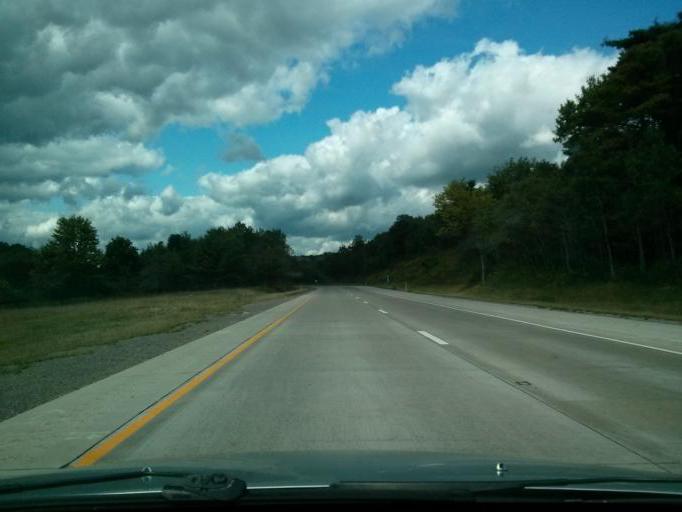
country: US
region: Pennsylvania
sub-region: Jefferson County
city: Falls Creek
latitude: 41.1574
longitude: -78.8194
